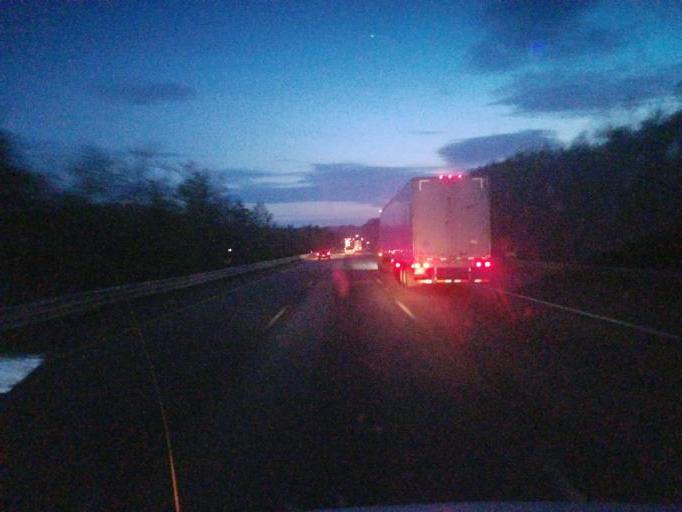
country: US
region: Massachusetts
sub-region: Worcester County
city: Berlin
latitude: 42.3964
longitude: -71.6068
